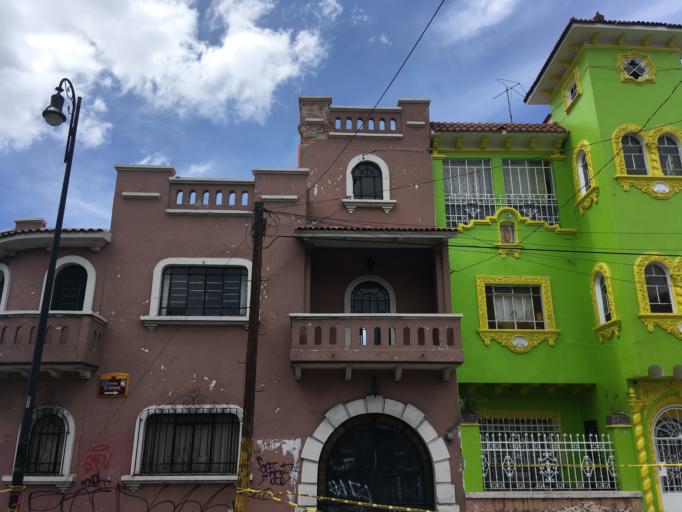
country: MX
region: Puebla
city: Puebla
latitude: 19.0468
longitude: -98.1898
